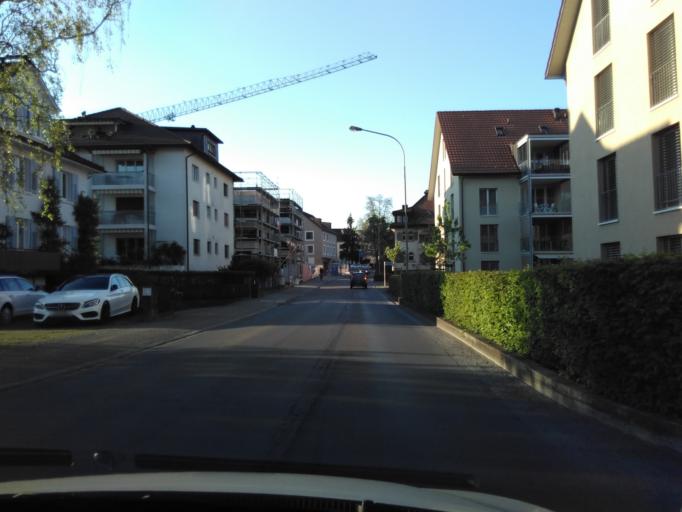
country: CH
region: Zurich
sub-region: Bezirk Hinwil
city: Rueti
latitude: 47.2570
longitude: 8.8515
